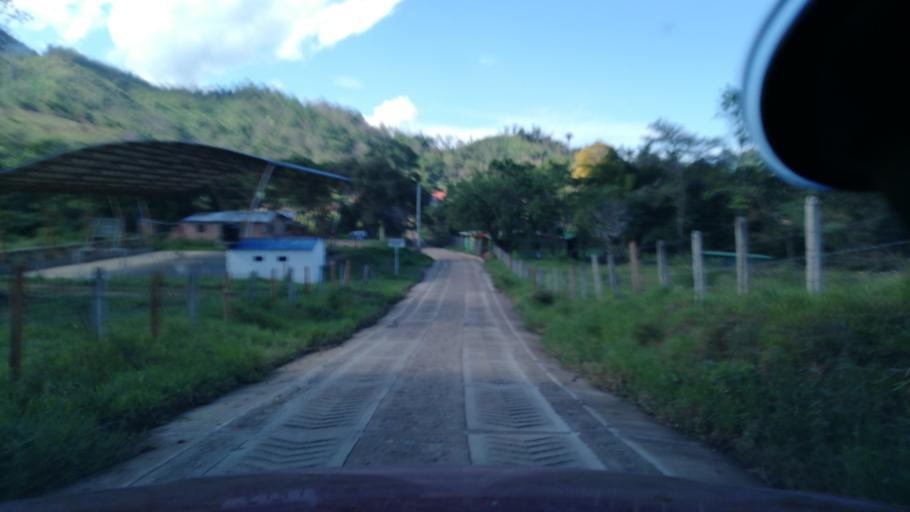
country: CO
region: Cundinamarca
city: Quipile
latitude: 4.7728
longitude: -74.6135
